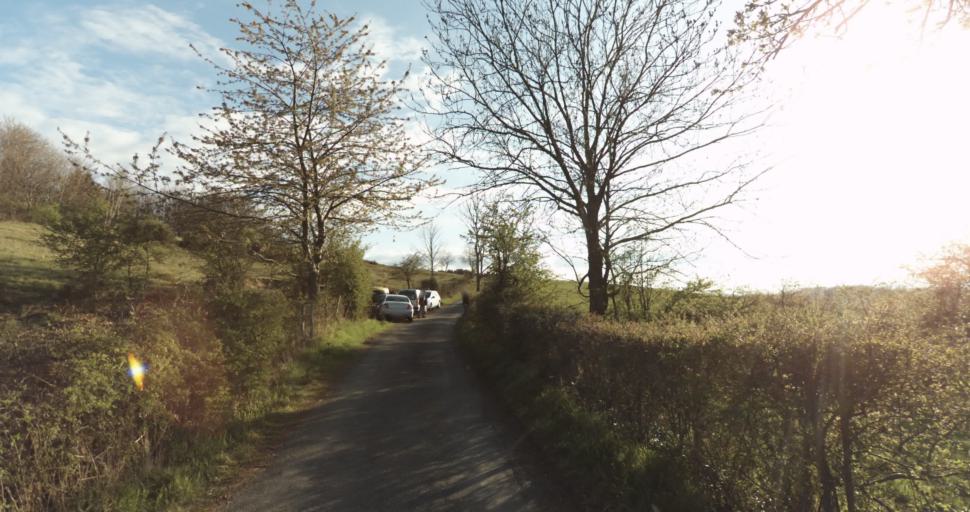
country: FR
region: Rhone-Alpes
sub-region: Departement de la Loire
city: Saint-Jean-Bonnefonds
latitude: 45.4654
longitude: 4.4478
